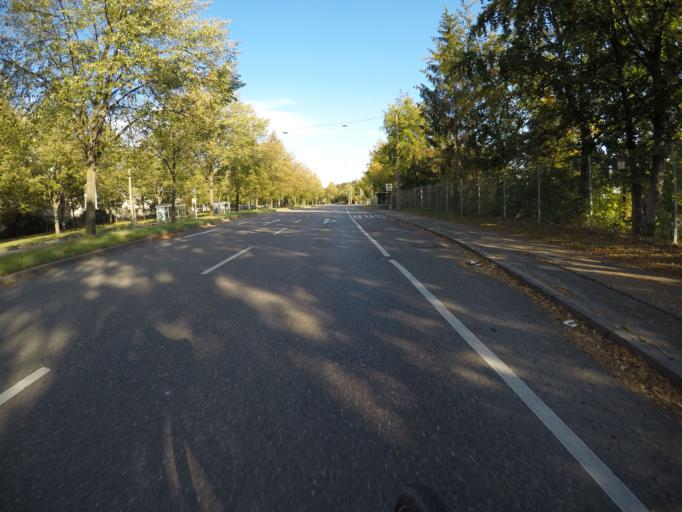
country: DE
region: Baden-Wuerttemberg
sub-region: Regierungsbezirk Stuttgart
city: Leinfelden-Echterdingen
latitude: 48.7221
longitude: 9.1675
